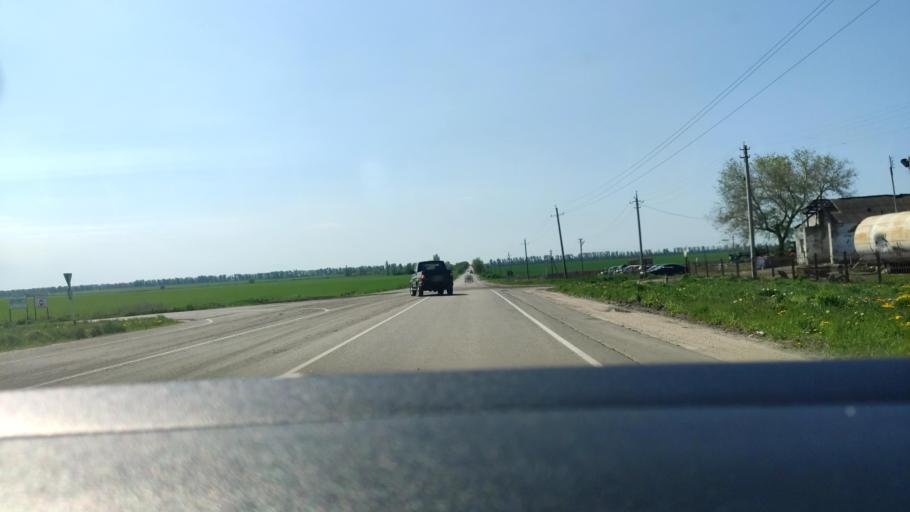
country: RU
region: Voronezj
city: Novaya Usman'
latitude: 51.5810
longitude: 39.3746
